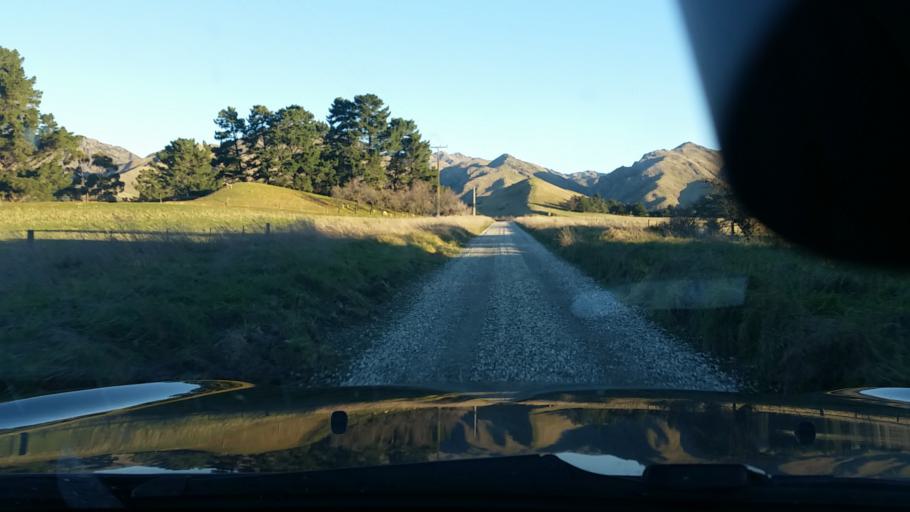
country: NZ
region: Marlborough
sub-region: Marlborough District
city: Blenheim
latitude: -41.7266
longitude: 174.0380
